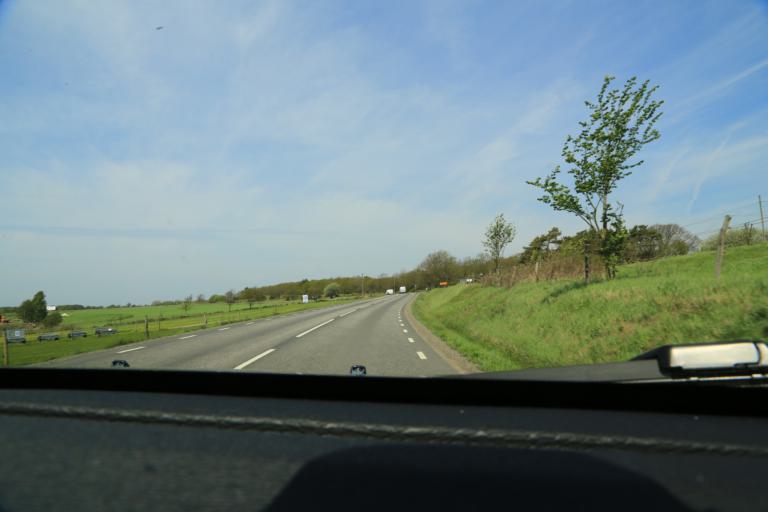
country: SE
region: Halland
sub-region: Varbergs Kommun
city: Traslovslage
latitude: 57.1099
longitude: 12.3251
